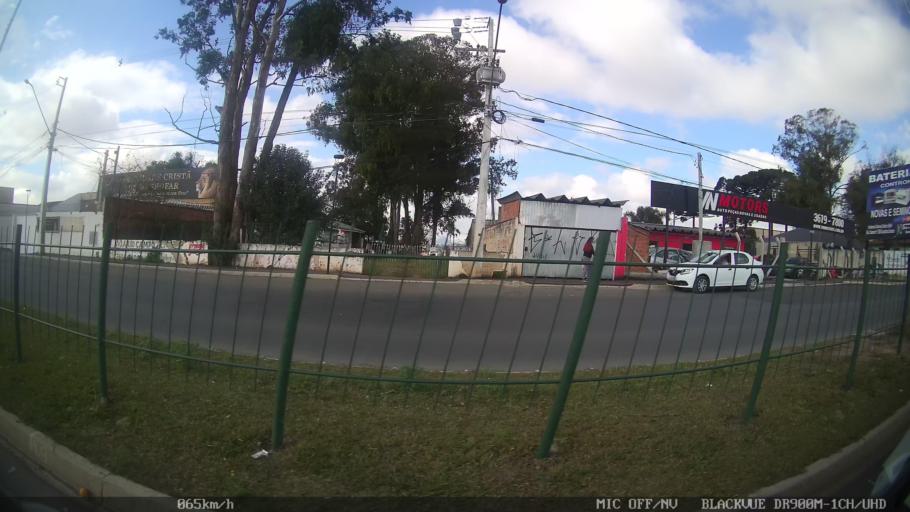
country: BR
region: Parana
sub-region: Pinhais
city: Pinhais
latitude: -25.3730
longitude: -49.1866
